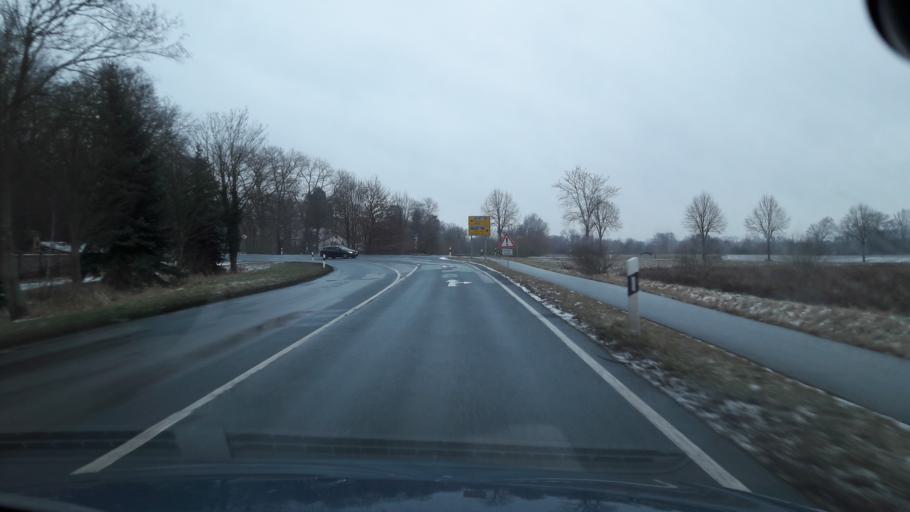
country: DE
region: North Rhine-Westphalia
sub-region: Regierungsbezirk Arnsberg
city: Lippstadt
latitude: 51.6845
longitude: 8.2946
